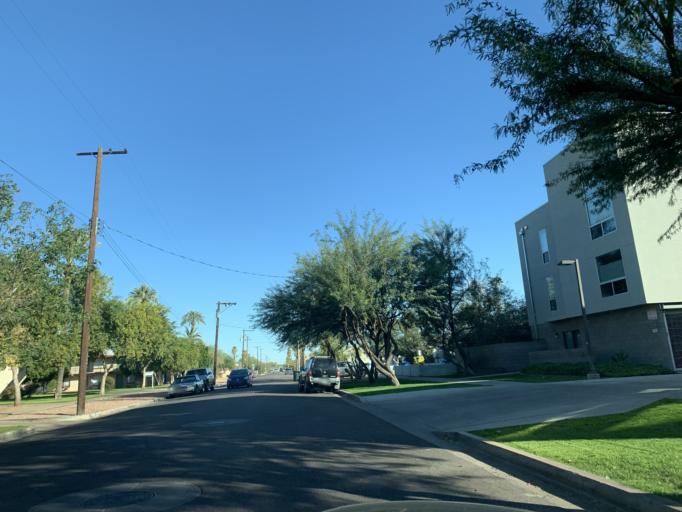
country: US
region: Arizona
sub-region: Maricopa County
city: Phoenix
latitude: 33.4599
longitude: -112.0638
